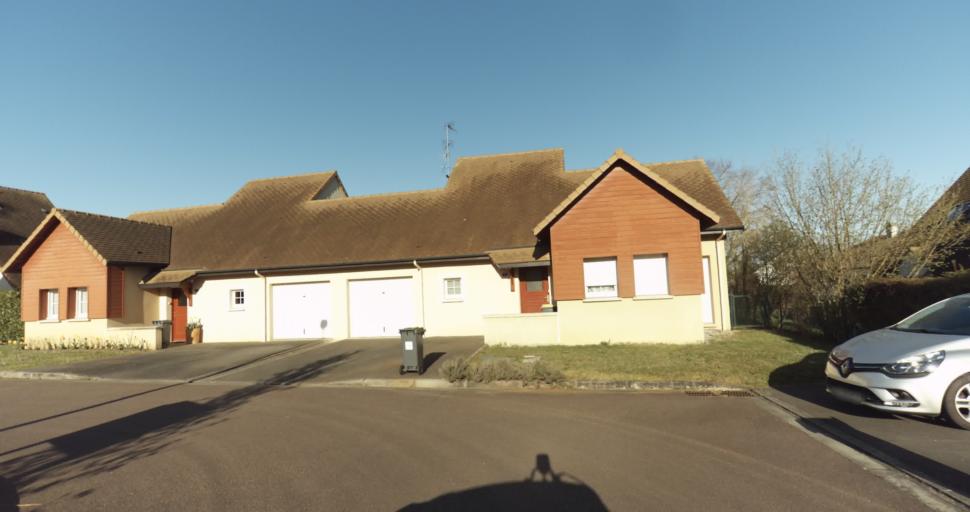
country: FR
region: Lower Normandy
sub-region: Departement du Calvados
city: Saint-Pierre-sur-Dives
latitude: 49.0219
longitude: -0.0247
